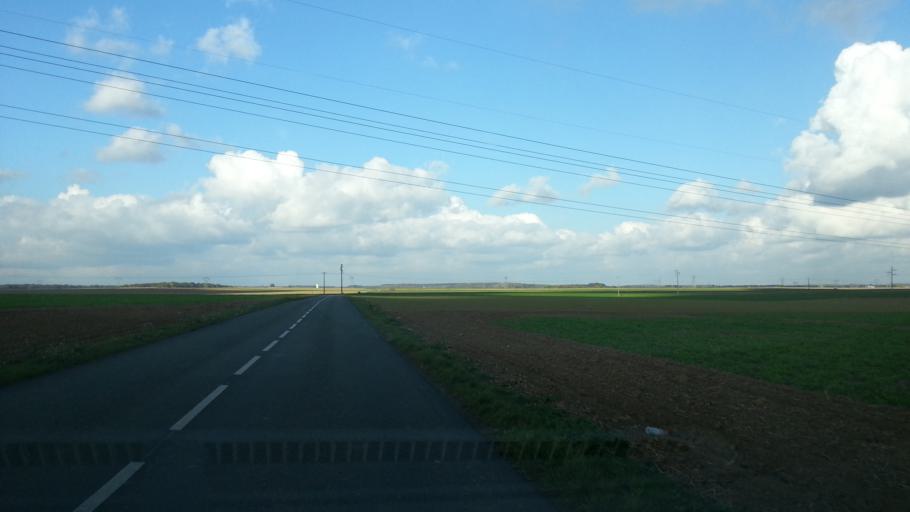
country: FR
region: Picardie
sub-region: Departement de l'Oise
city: Villers-sous-Saint-Leu
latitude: 49.2302
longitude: 2.4129
